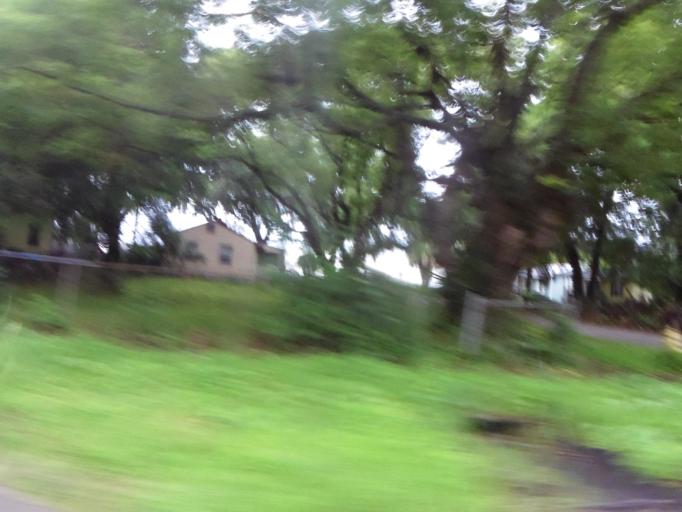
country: US
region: Florida
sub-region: Duval County
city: Jacksonville
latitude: 30.3308
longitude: -81.6343
